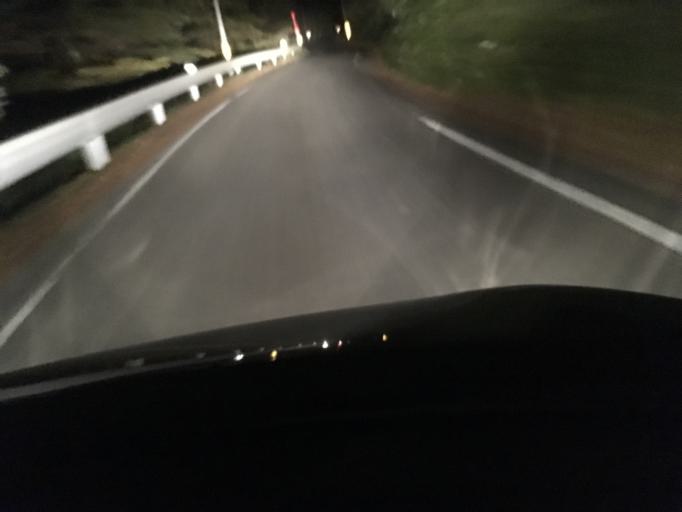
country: JP
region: Miyagi
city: Furukawa
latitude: 38.8260
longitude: 140.7952
